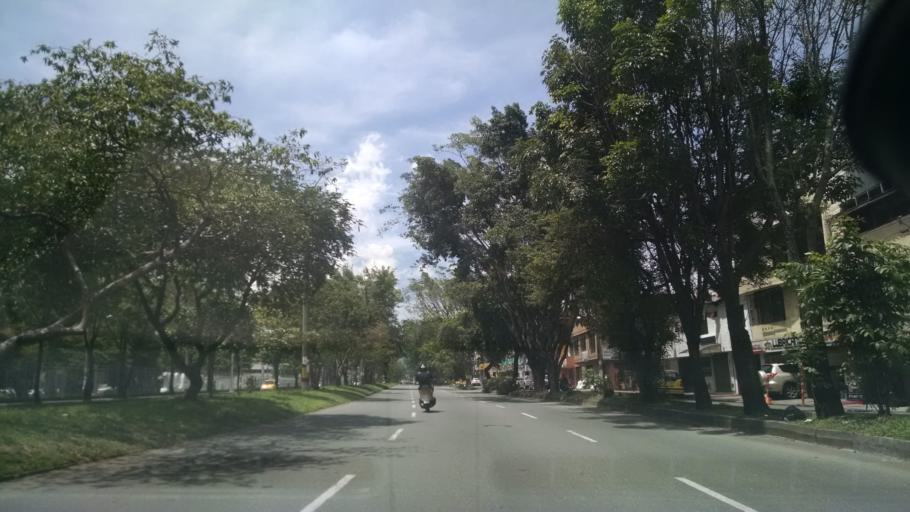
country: CO
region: Antioquia
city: Itagui
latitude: 6.2104
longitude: -75.5846
